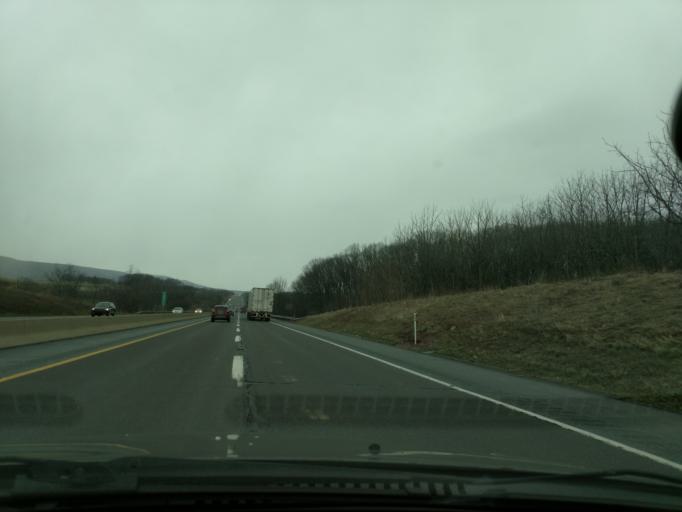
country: US
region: Pennsylvania
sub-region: Berks County
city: West Hamburg
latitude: 40.5411
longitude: -76.0406
